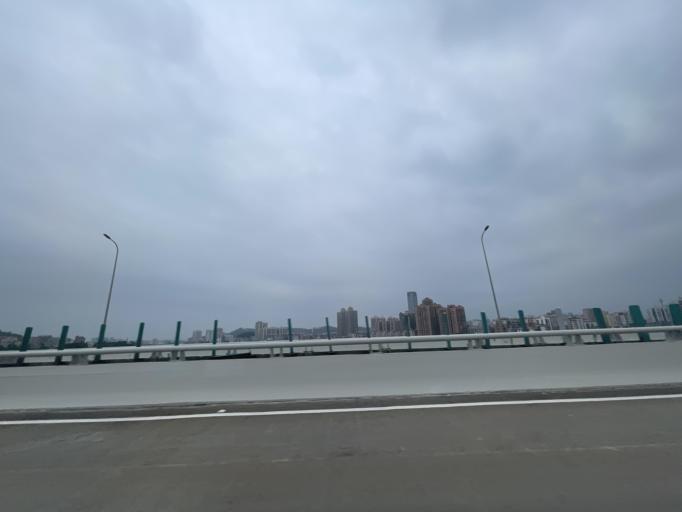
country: CN
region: Guangdong
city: Humen
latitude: 22.8067
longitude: 113.6658
